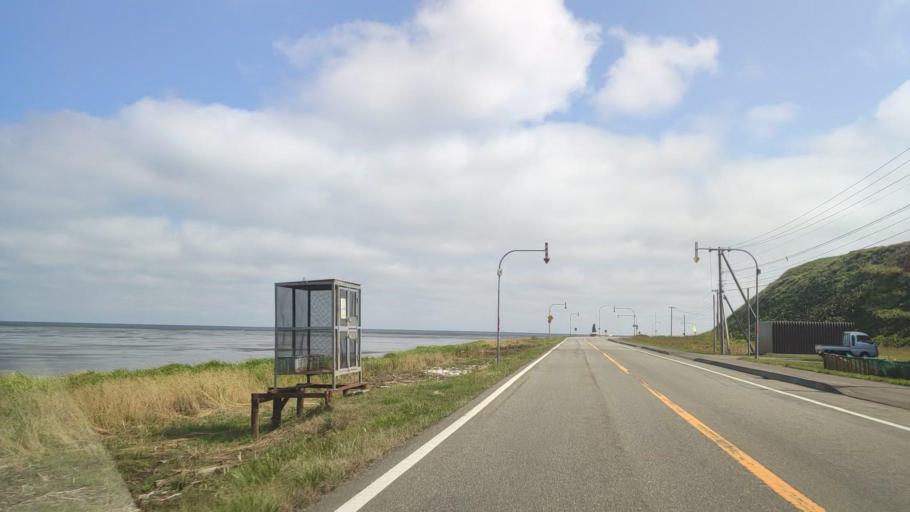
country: JP
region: Hokkaido
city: Makubetsu
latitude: 45.5129
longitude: 141.9018
